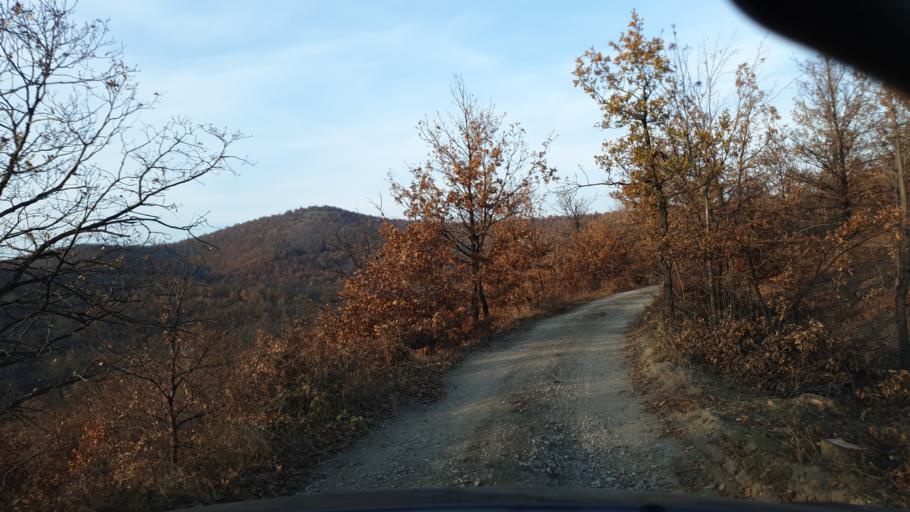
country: RS
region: Central Serbia
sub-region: Borski Okrug
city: Bor
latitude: 44.0692
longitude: 22.0744
